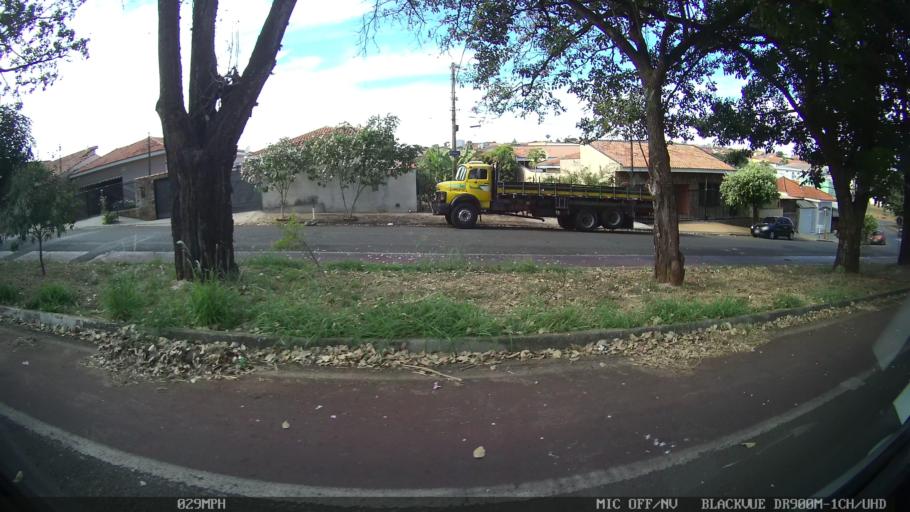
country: BR
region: Sao Paulo
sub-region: Catanduva
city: Catanduva
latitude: -21.1185
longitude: -48.9699
